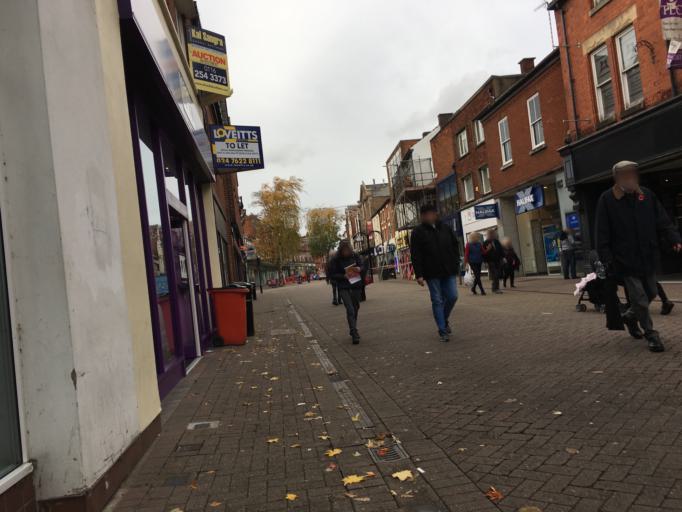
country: GB
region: England
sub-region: Warwickshire
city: Nuneaton
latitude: 52.5232
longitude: -1.4685
